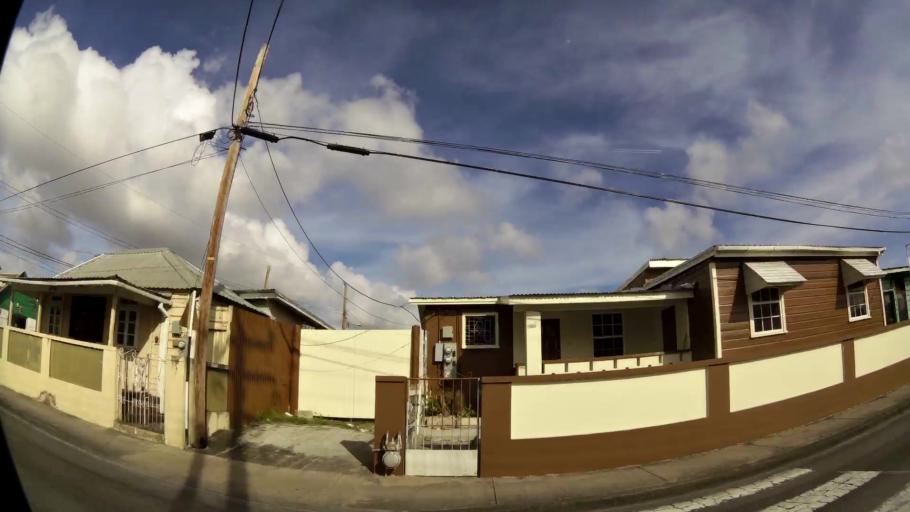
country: BB
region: Saint Michael
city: Bridgetown
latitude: 13.0893
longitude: -59.6014
